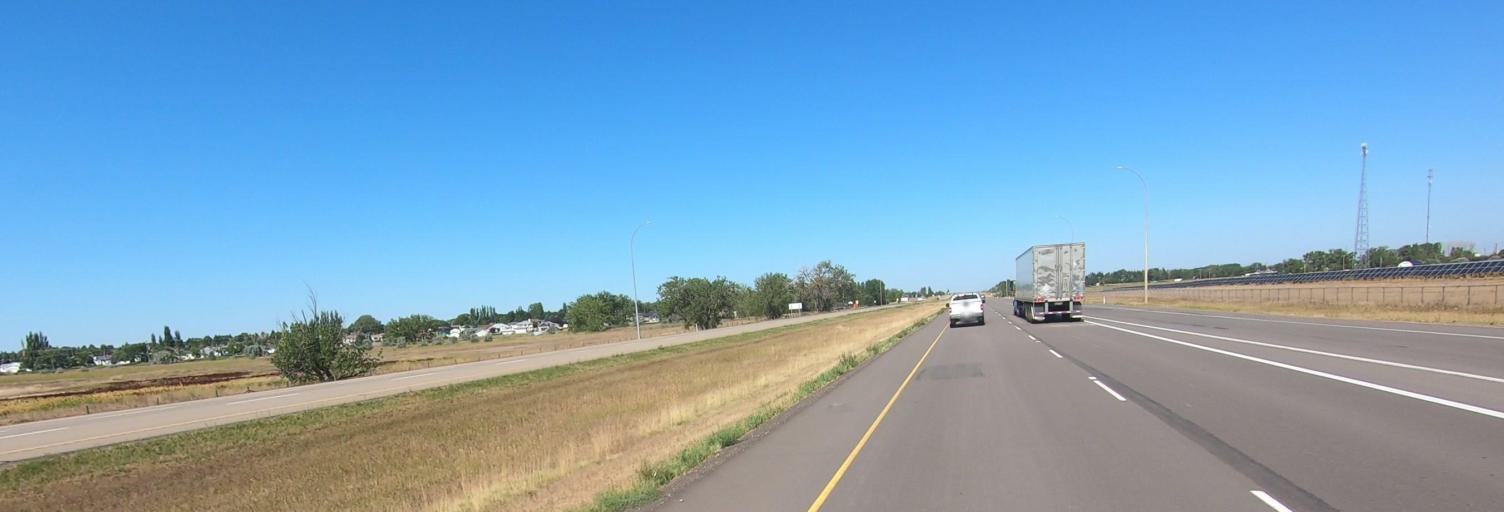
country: CA
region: Alberta
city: Brooks
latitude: 50.5756
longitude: -111.8685
